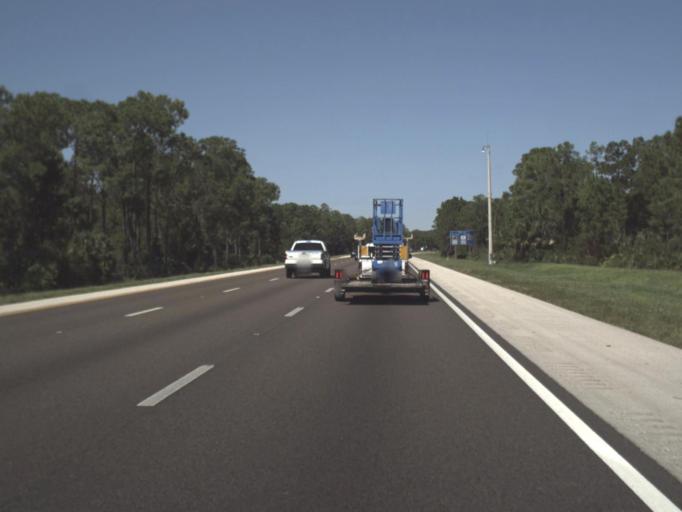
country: US
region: Florida
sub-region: Collier County
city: Vineyards
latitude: 26.2565
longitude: -81.7405
